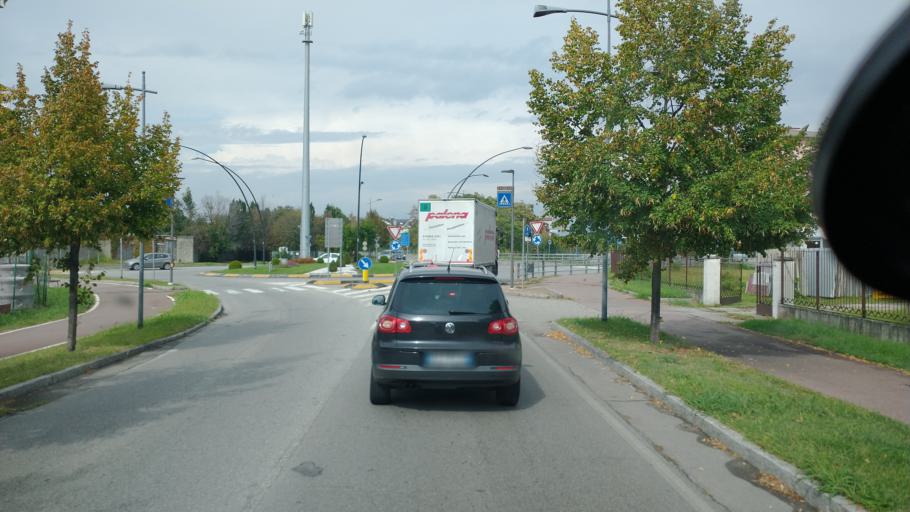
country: IT
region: Lombardy
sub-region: Provincia di Bergamo
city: Treviglio
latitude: 45.5215
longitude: 9.6060
